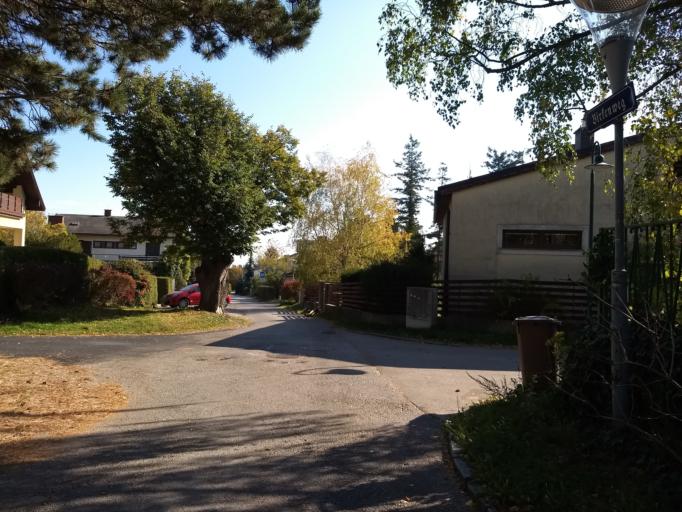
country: AT
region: Lower Austria
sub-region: Politischer Bezirk Modling
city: Giesshubl
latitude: 48.1037
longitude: 16.2394
